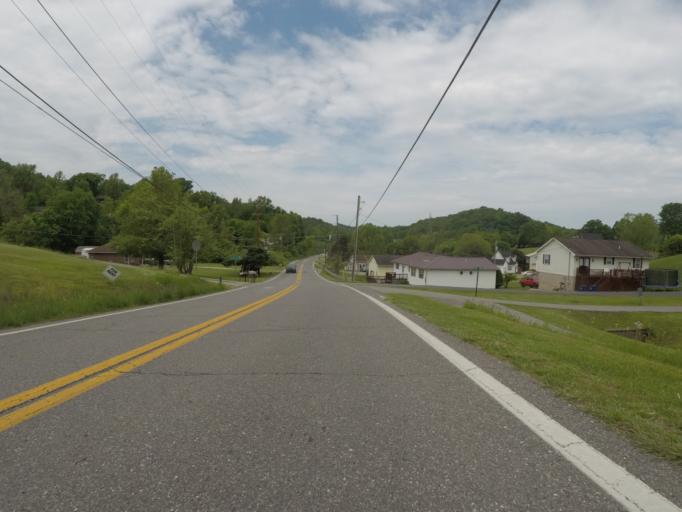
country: US
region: West Virginia
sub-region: Wayne County
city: Ceredo
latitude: 38.3569
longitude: -82.5273
